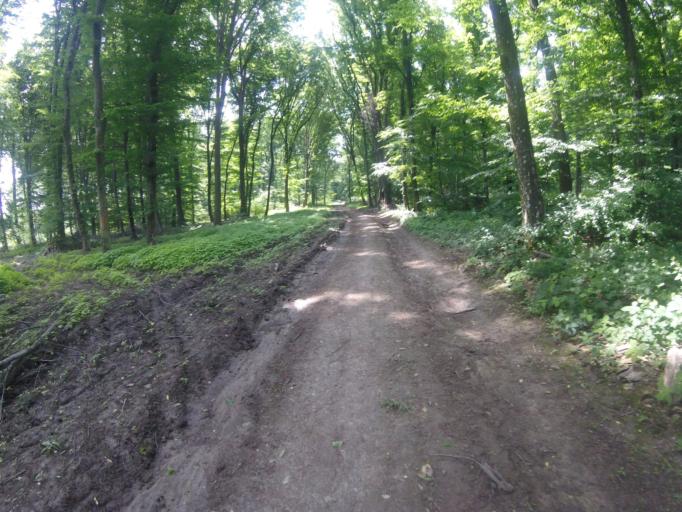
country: HU
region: Zala
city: Cserszegtomaj
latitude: 46.9094
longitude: 17.1928
